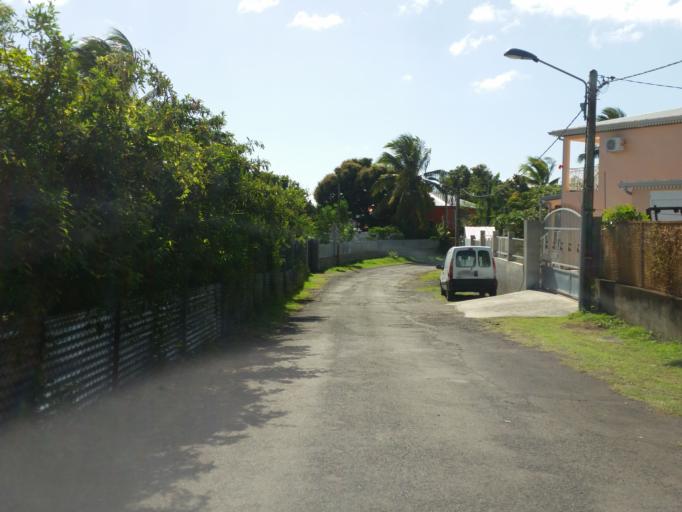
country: RE
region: Reunion
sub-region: Reunion
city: Sainte-Marie
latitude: -20.8960
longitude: 55.5303
